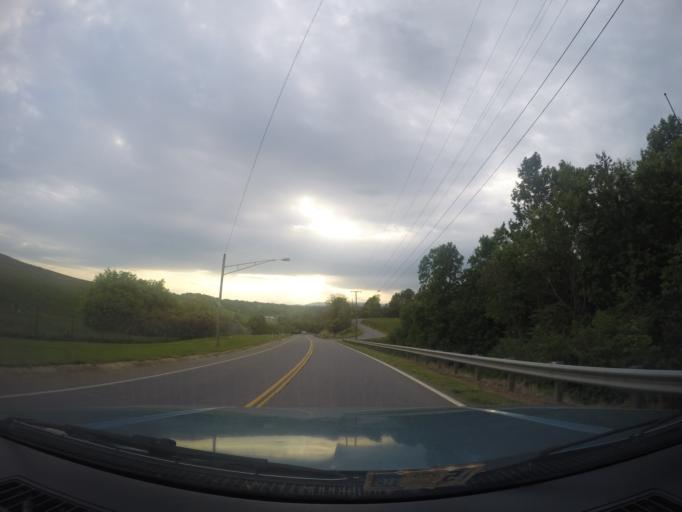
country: US
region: Virginia
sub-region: Amherst County
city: Madison Heights
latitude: 37.3943
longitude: -79.1052
